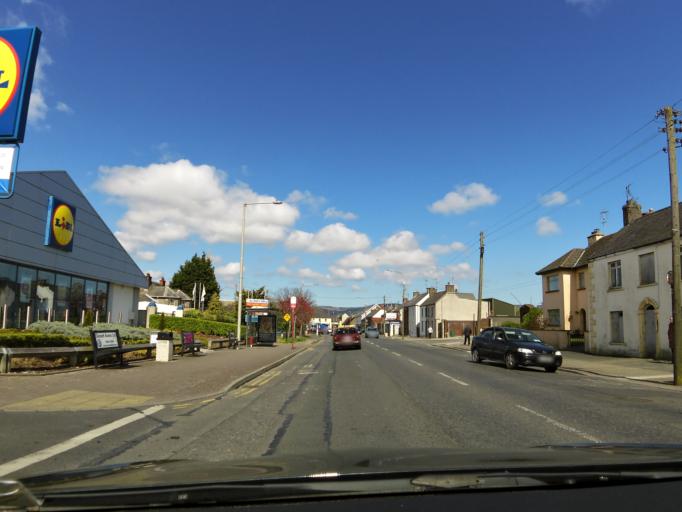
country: IE
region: Leinster
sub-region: Wicklow
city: Arklow
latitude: 52.7953
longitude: -6.1626
